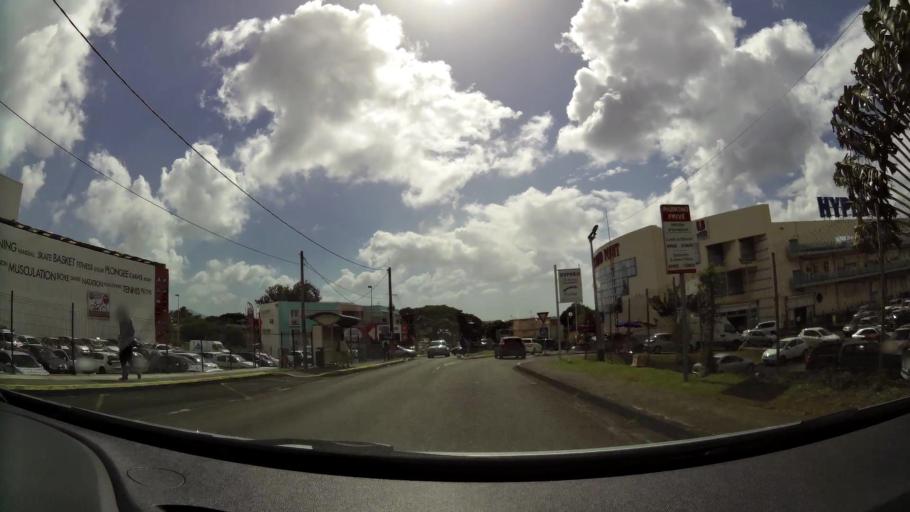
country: MQ
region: Martinique
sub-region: Martinique
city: Fort-de-France
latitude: 14.6042
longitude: -61.0880
